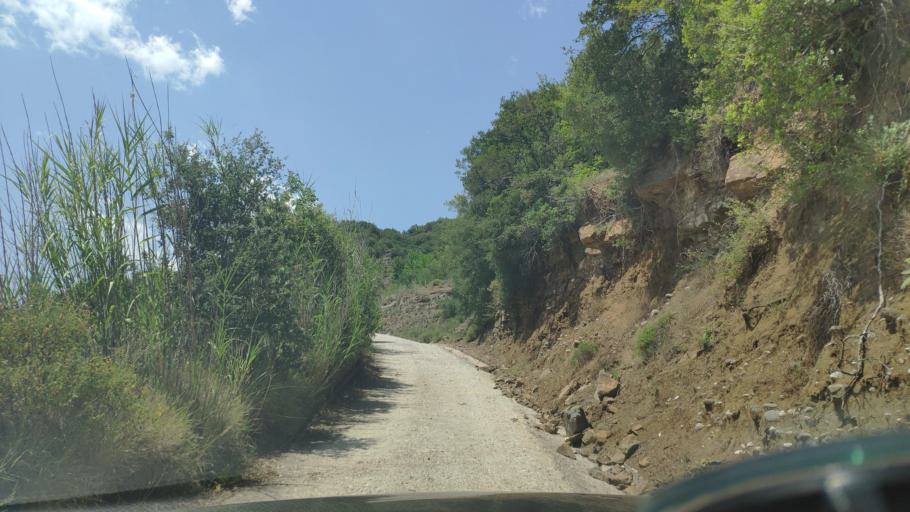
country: GR
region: Thessaly
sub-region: Nomos Kardhitsas
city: Anthiro
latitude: 39.2473
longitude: 21.3896
